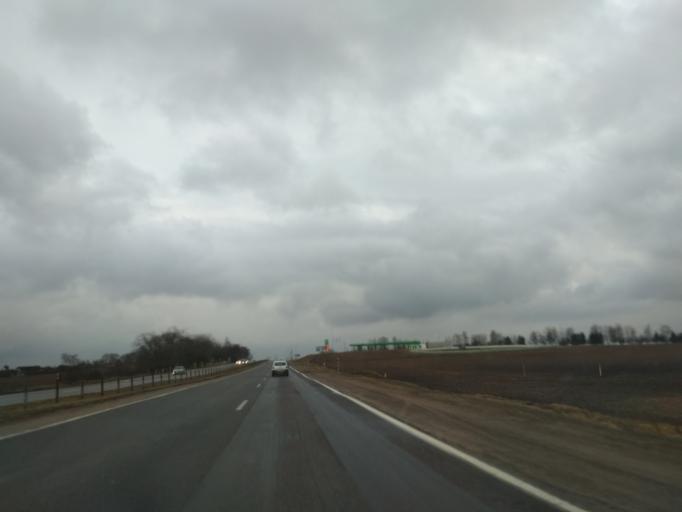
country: BY
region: Minsk
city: Dukora
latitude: 53.7094
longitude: 27.8742
